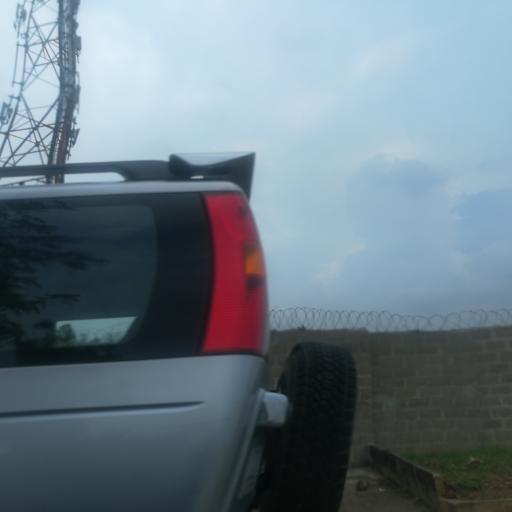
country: NG
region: Lagos
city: Ojota
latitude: 6.5801
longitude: 3.3843
